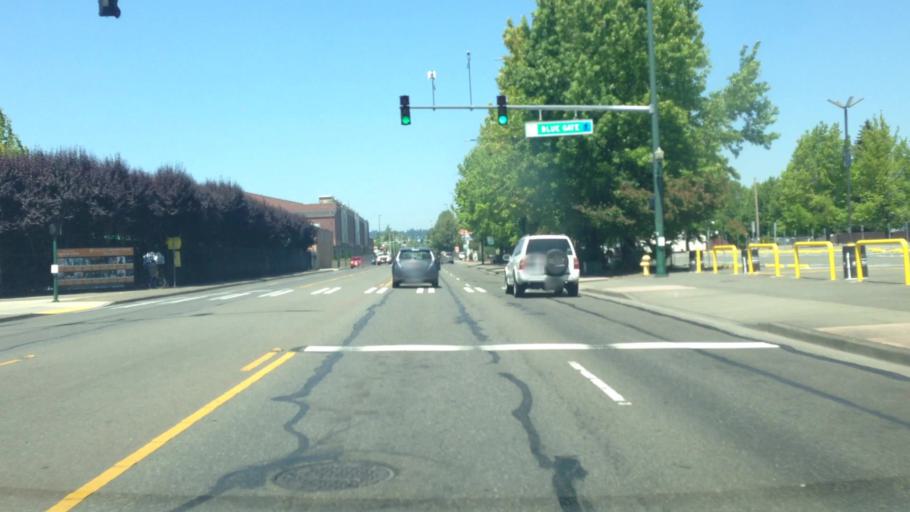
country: US
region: Washington
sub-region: Pierce County
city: Puyallup
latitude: 47.1815
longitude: -122.2936
